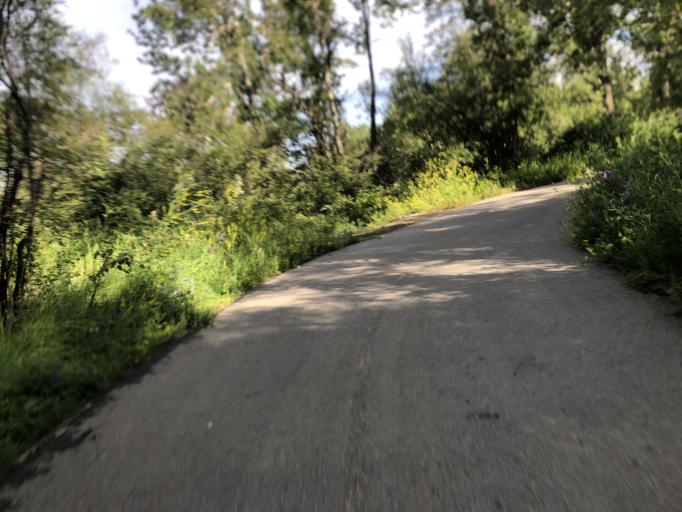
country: CA
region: Alberta
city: Calgary
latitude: 50.9991
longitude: -114.0246
